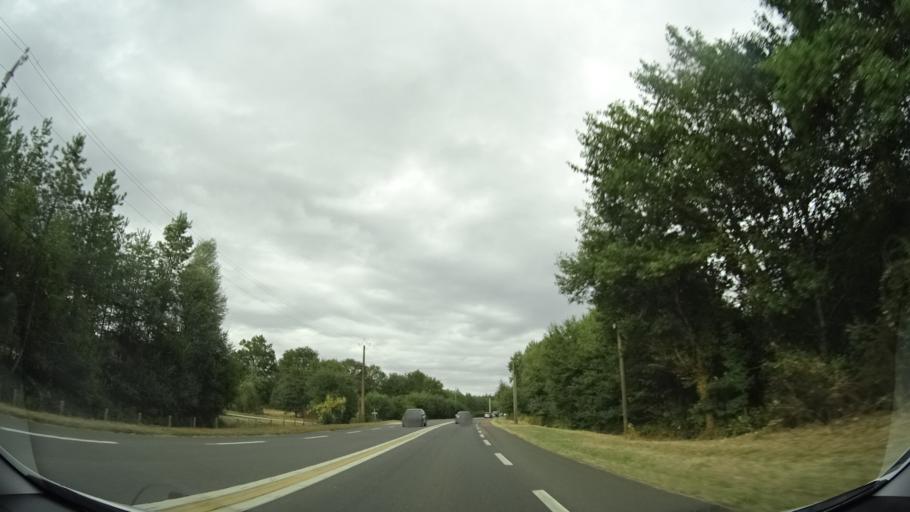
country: FR
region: Centre
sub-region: Departement du Loiret
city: Chateauneuf-sur-Loire
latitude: 47.8879
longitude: 2.2540
